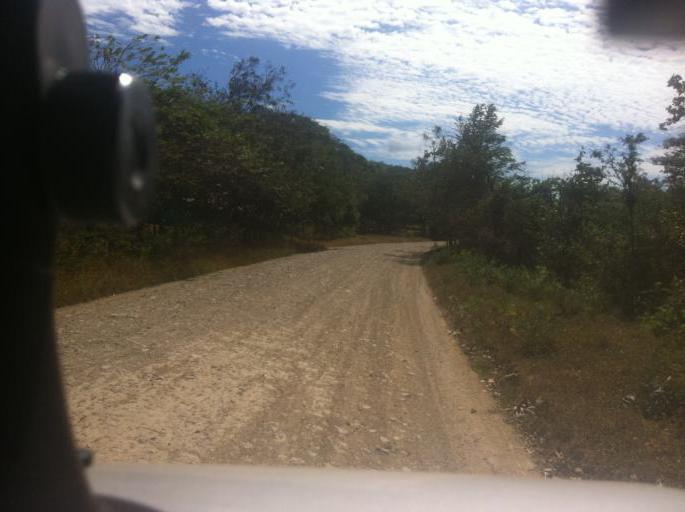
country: NI
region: Rivas
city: Tola
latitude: 11.5213
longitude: -86.0706
